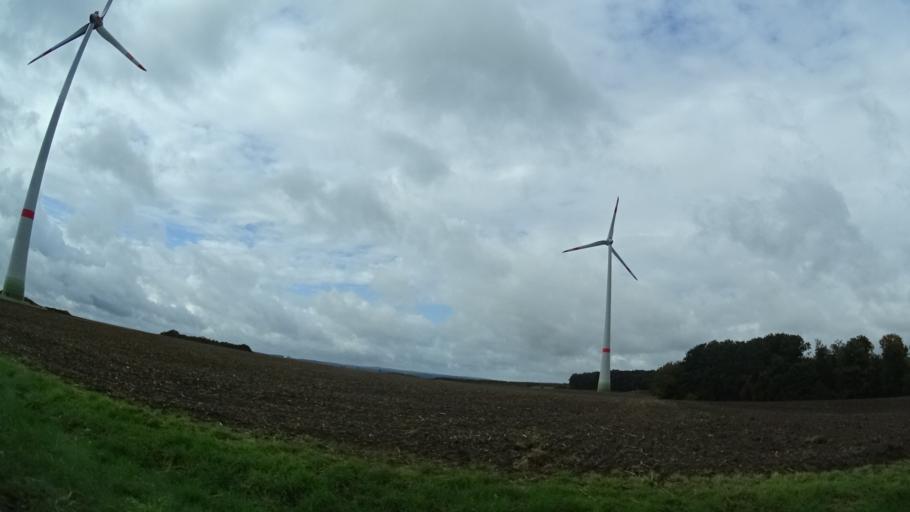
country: DE
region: Bavaria
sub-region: Upper Franconia
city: Priesendorf
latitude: 49.9106
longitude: 10.7378
